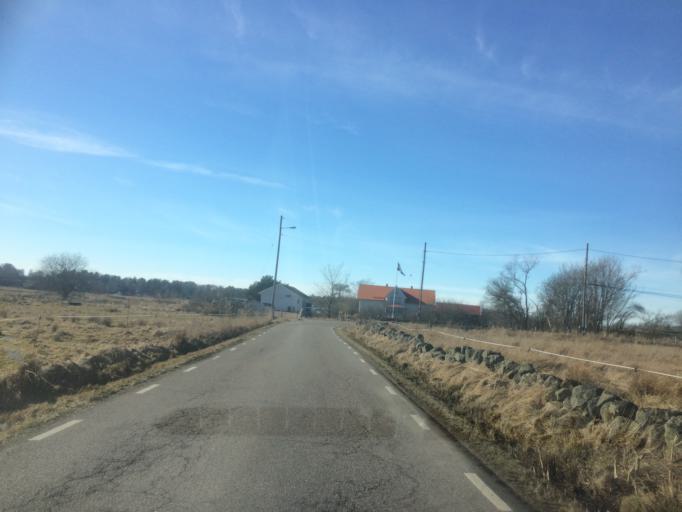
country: SE
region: Vaestra Goetaland
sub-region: Goteborg
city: Majorna
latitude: 57.7864
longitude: 11.8697
